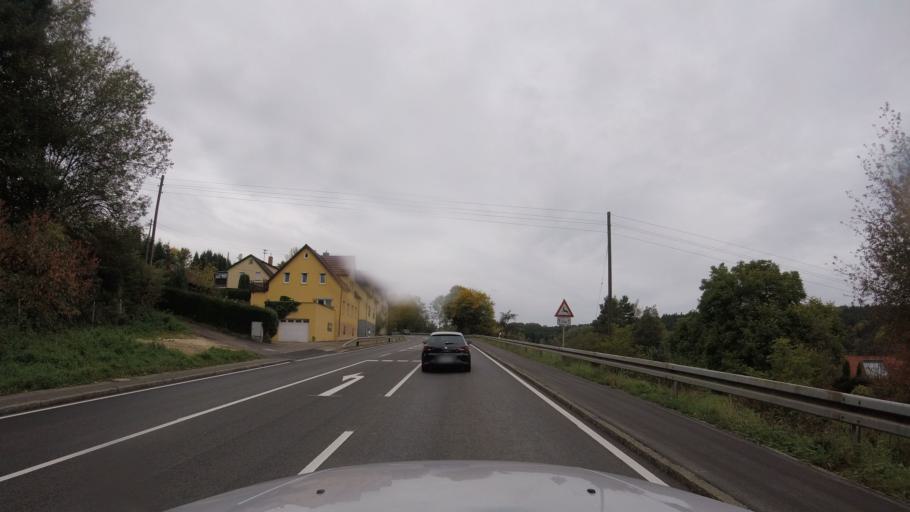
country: DE
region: Baden-Wuerttemberg
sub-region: Regierungsbezirk Stuttgart
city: Schwabisch Gmund
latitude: 48.8100
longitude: 9.7937
